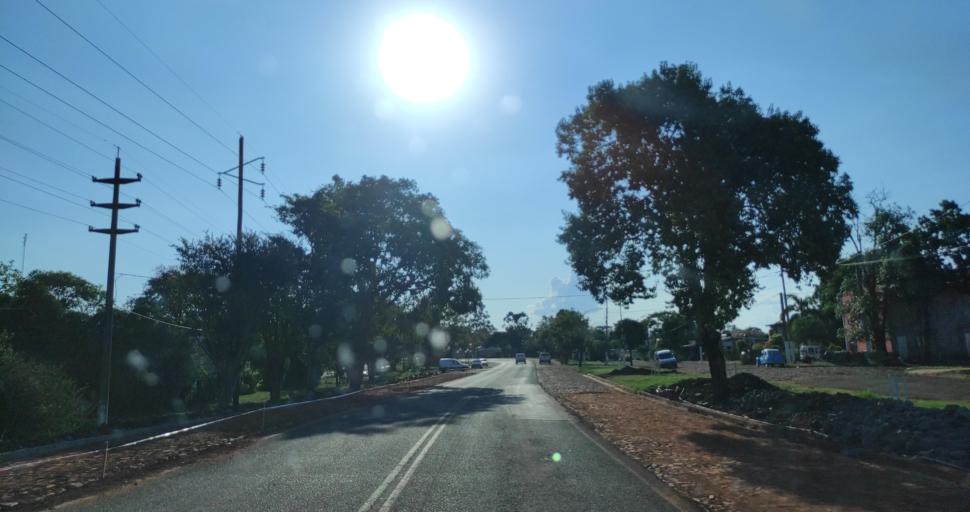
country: AR
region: Misiones
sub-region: Departamento de Eldorado
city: Eldorado
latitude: -26.4146
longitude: -54.4935
